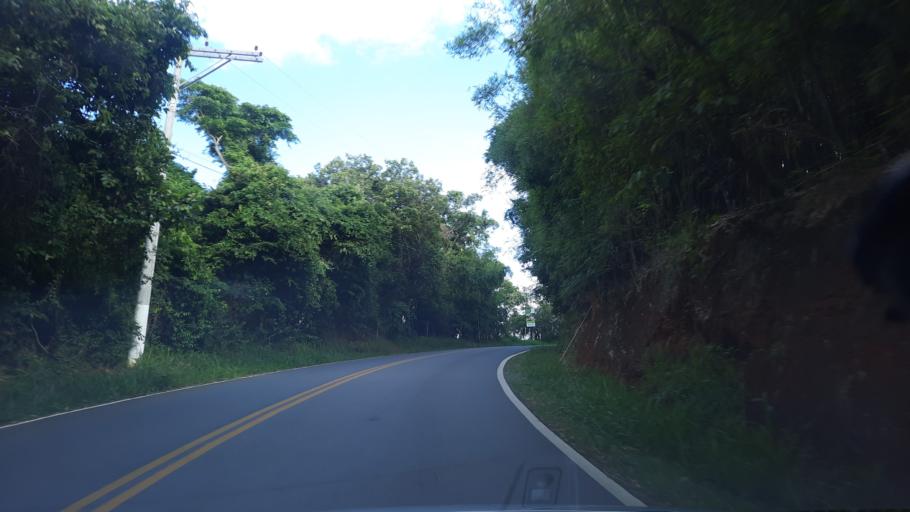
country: BR
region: Sao Paulo
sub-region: Atibaia
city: Atibaia
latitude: -23.0941
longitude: -46.5139
